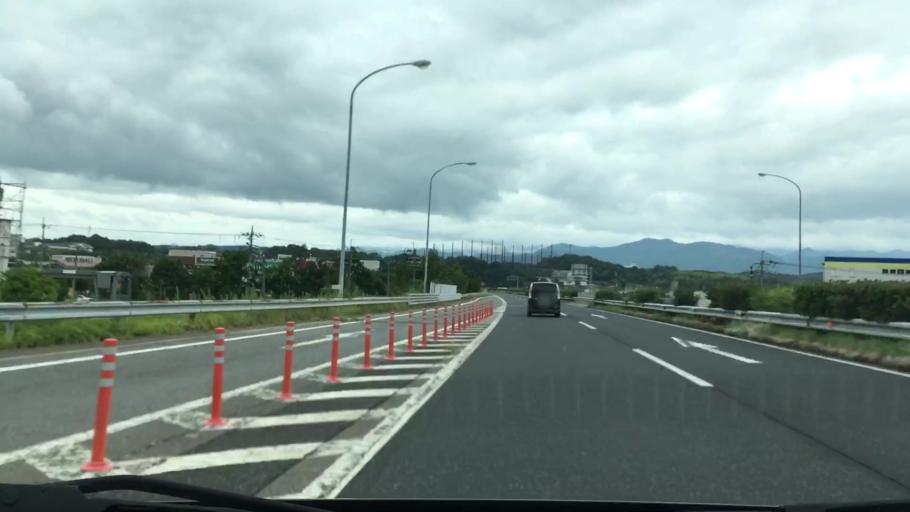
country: JP
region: Okayama
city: Tsuyama
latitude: 35.0638
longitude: 134.0500
